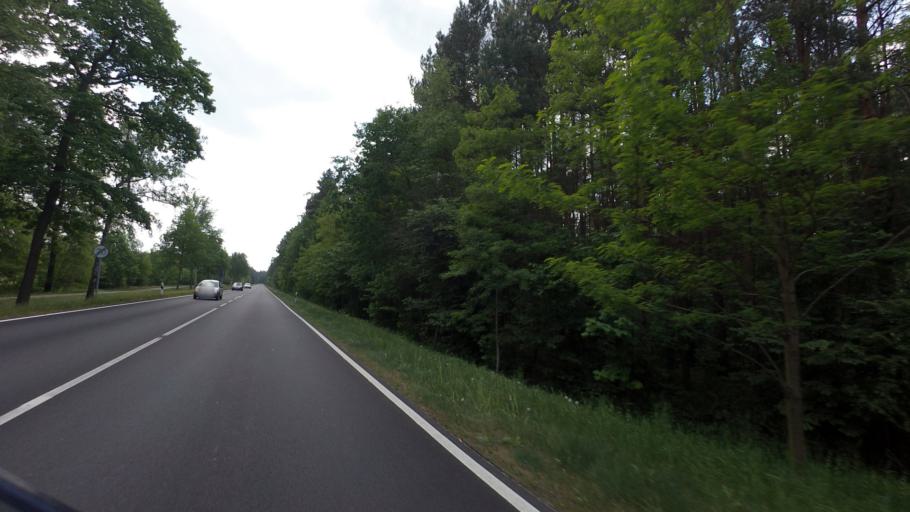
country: DE
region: Saxony
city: Rietschen
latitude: 51.3818
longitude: 14.7882
